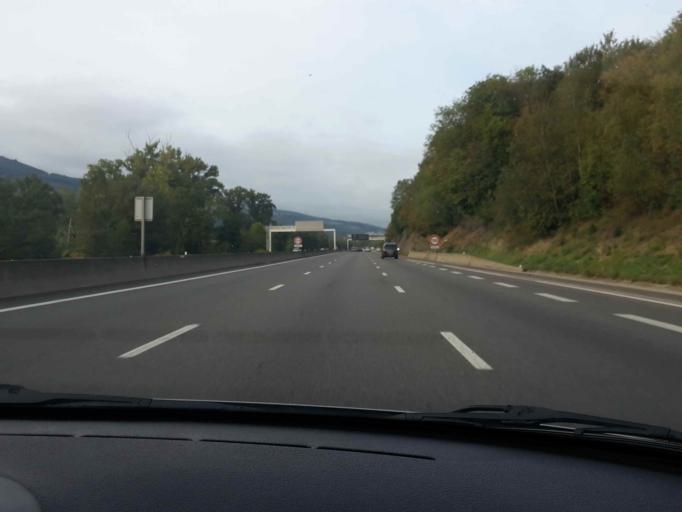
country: FR
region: Rhone-Alpes
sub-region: Departement de la Loire
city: Saint-Jean-Bonnefonds
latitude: 45.4556
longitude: 4.4815
